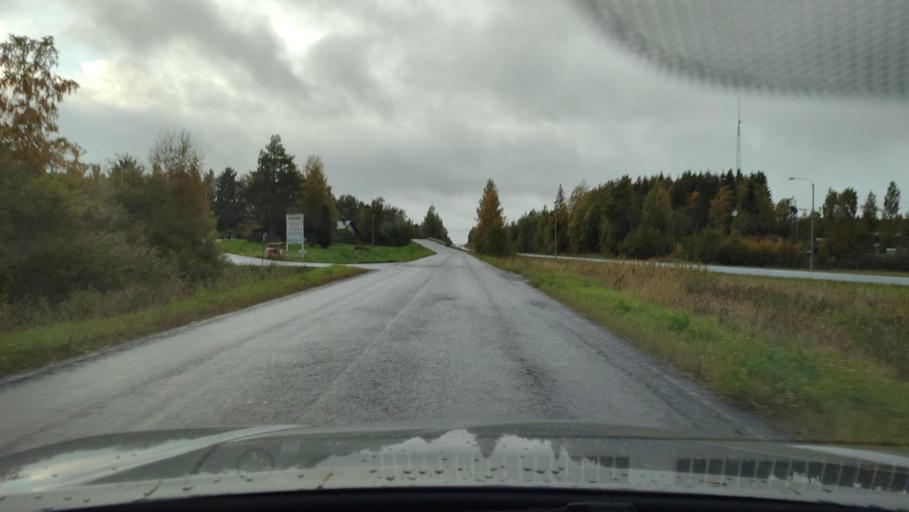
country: FI
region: Ostrobothnia
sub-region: Sydosterbotten
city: Kristinestad
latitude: 62.2674
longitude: 21.4758
